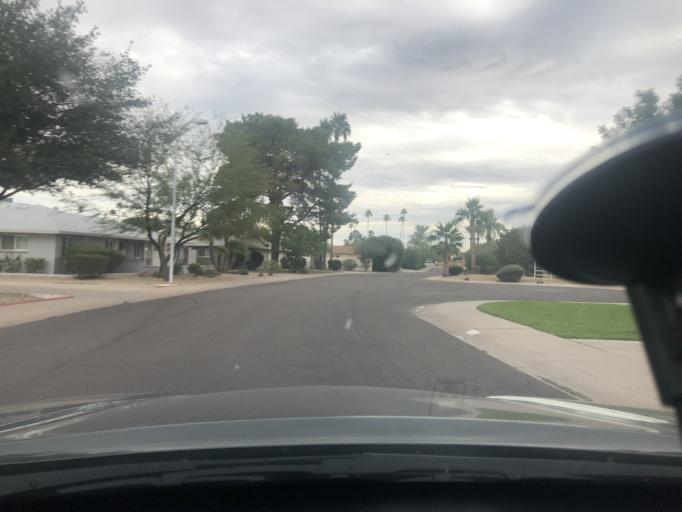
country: US
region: Arizona
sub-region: Maricopa County
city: Scottsdale
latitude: 33.4821
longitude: -111.9030
